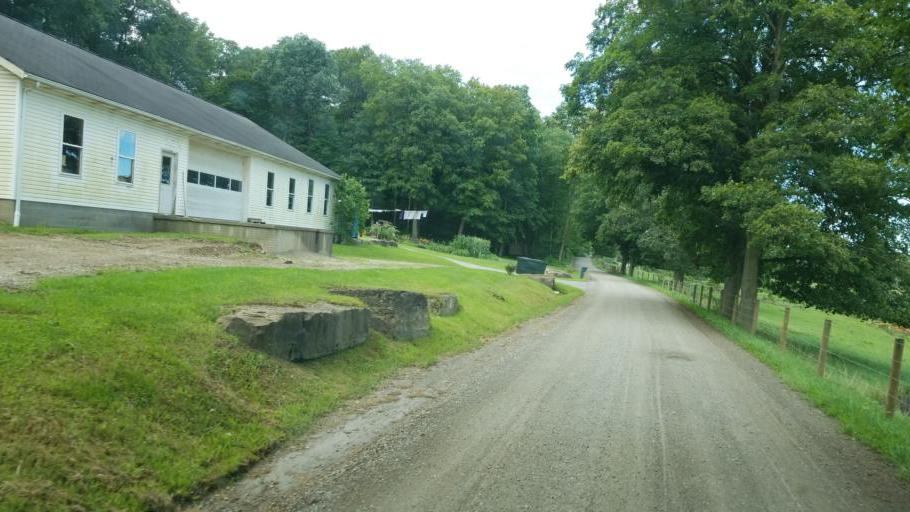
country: US
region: Ohio
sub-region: Holmes County
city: Millersburg
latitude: 40.4864
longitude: -81.8527
